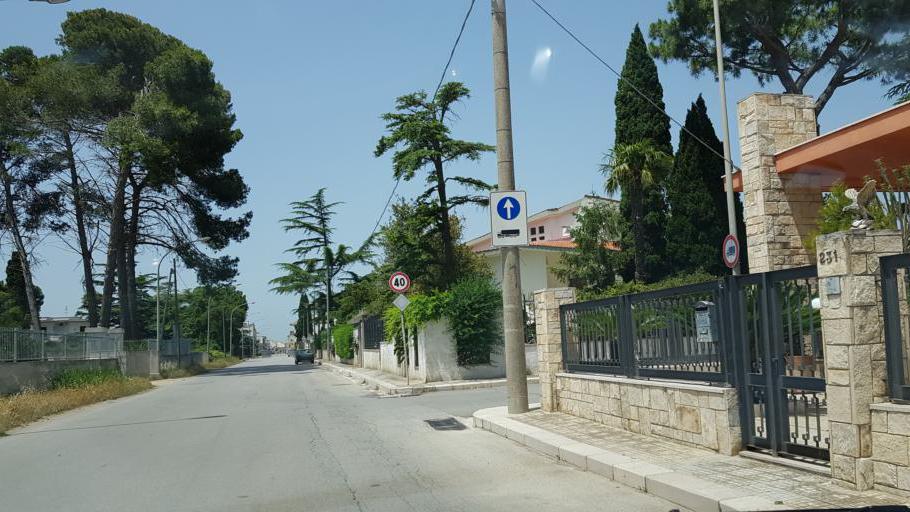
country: IT
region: Apulia
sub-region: Provincia di Brindisi
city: Mesagne
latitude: 40.5504
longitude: 17.8163
